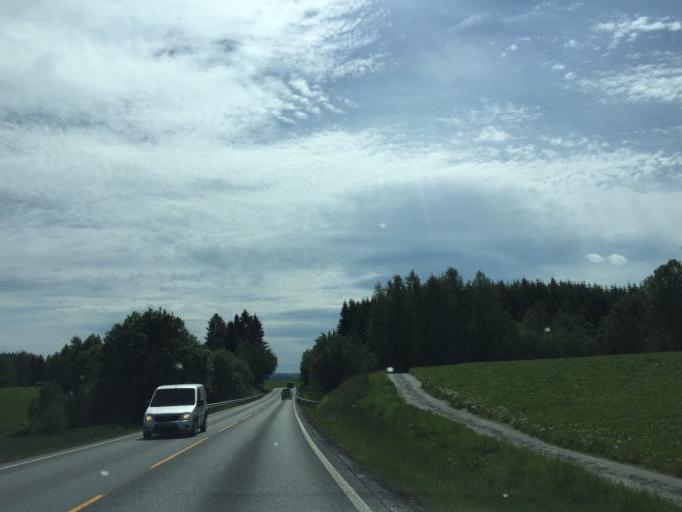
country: NO
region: Akershus
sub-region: Nes
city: Arnes
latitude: 60.1370
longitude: 11.4331
